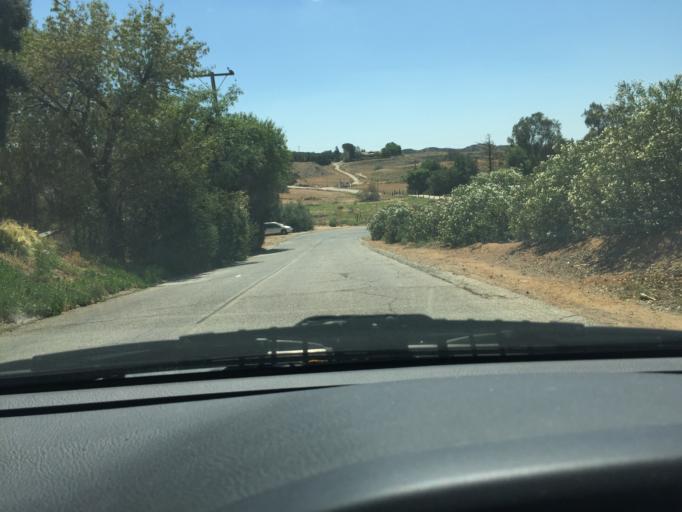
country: US
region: California
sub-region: Riverside County
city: Calimesa
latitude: 34.0001
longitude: -117.0258
